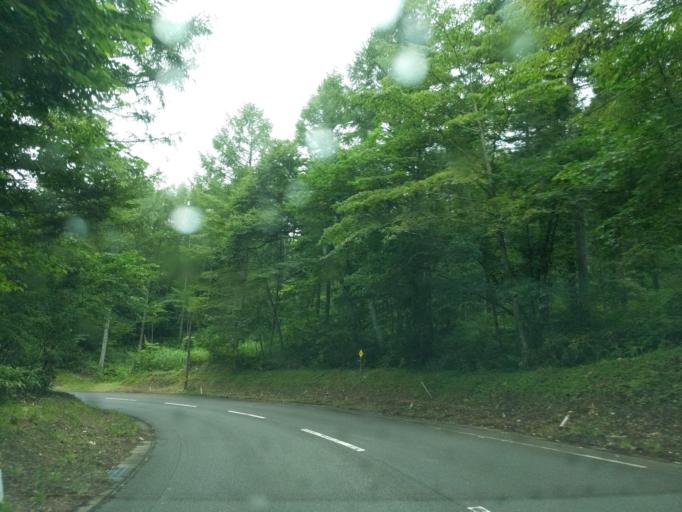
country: JP
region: Fukushima
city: Sukagawa
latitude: 37.2604
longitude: 140.0964
